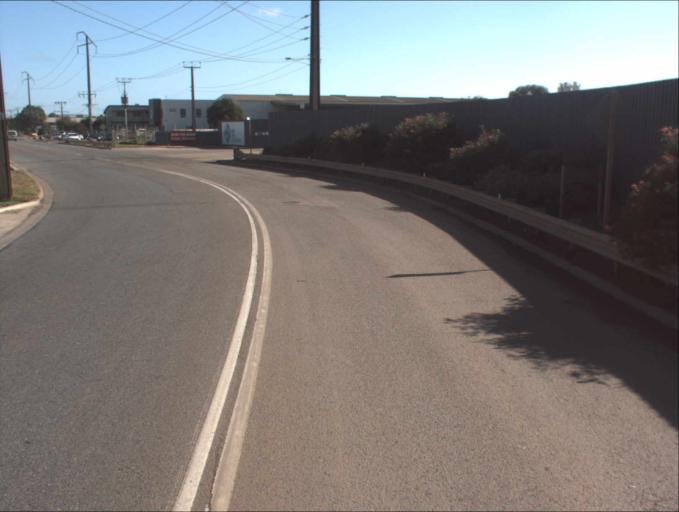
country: AU
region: South Australia
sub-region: Port Adelaide Enfield
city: Alberton
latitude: -34.8407
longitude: 138.5384
